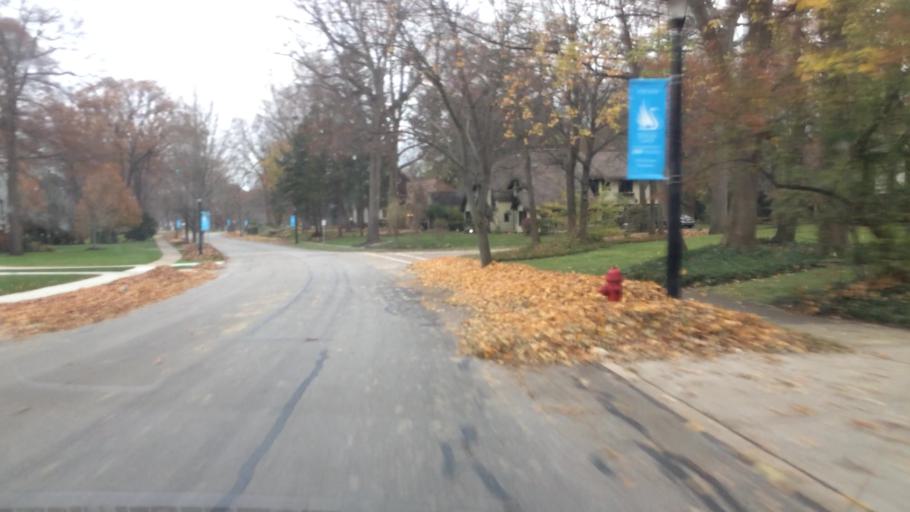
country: US
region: Ohio
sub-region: Summit County
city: Silver Lake
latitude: 41.1552
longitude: -81.4627
